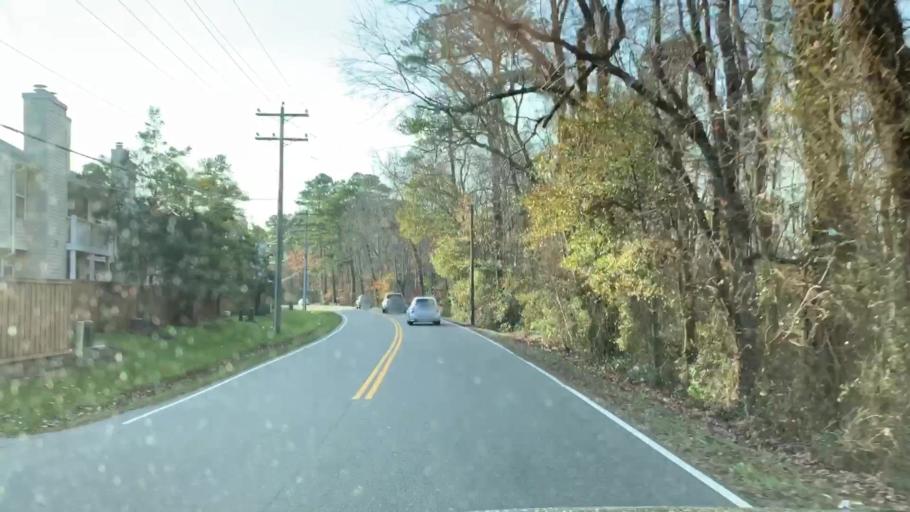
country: US
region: Virginia
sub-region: City of Chesapeake
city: Chesapeake
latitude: 36.7815
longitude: -76.1587
